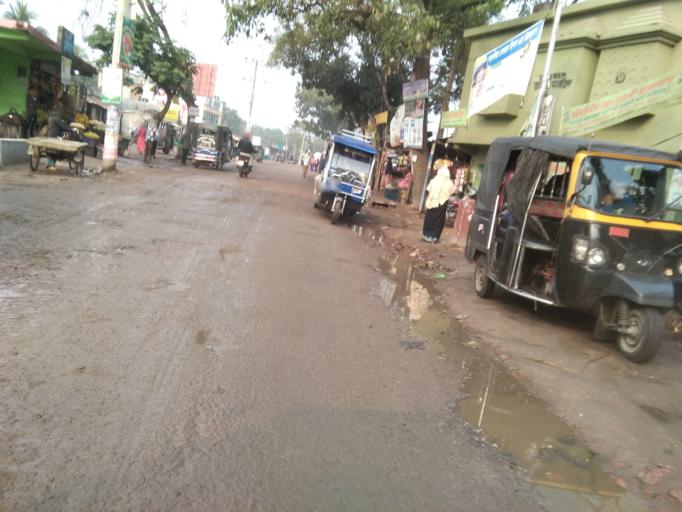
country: IN
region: West Bengal
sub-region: North 24 Parganas
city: Taki
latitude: 22.6401
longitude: 88.9876
